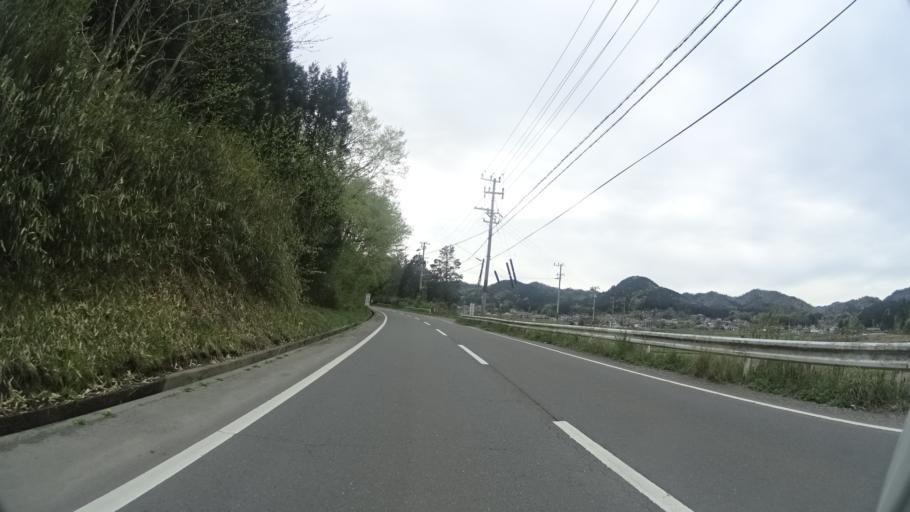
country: JP
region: Kyoto
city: Ayabe
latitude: 35.1854
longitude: 135.4238
